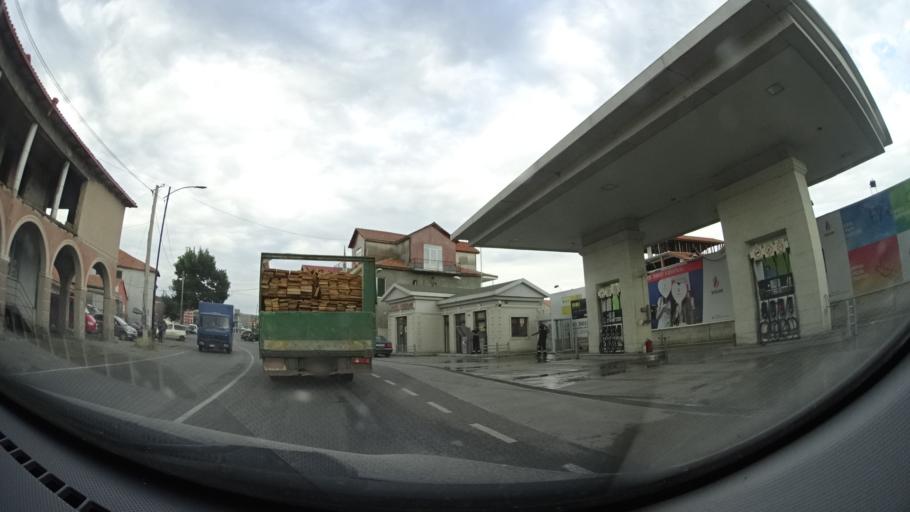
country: GE
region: Samtskhe-Javakheti
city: Akhaltsikhe
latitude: 41.6415
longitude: 42.9807
